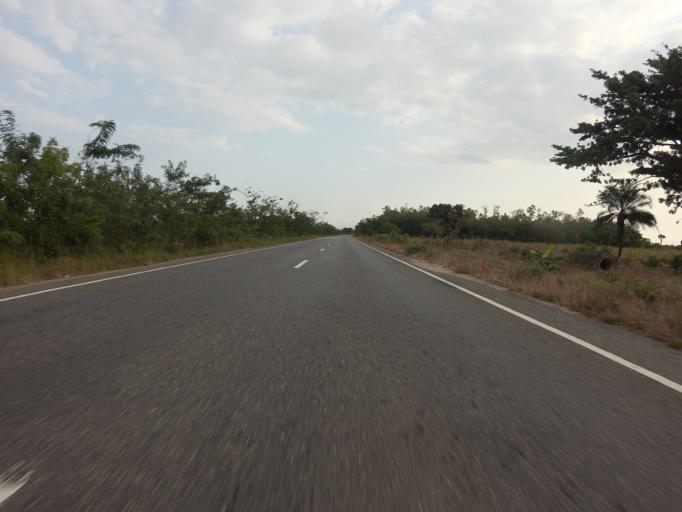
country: GH
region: Volta
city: Ho
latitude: 6.1231
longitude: 0.5213
